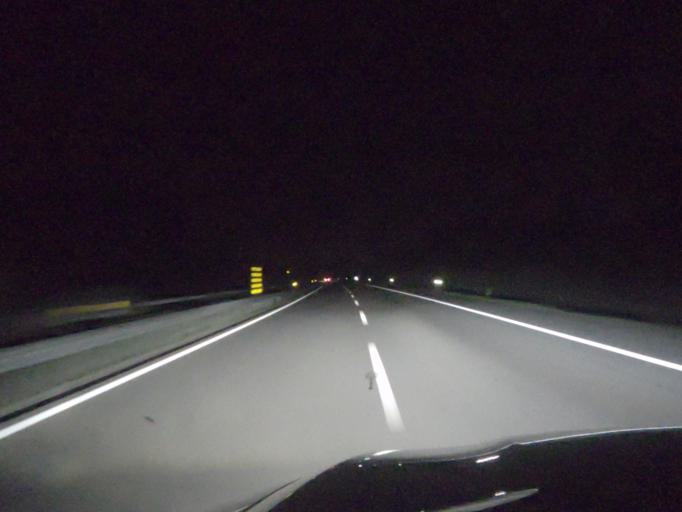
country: PT
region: Aveiro
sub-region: Anadia
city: Arcos
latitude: 40.4307
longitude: -8.5030
